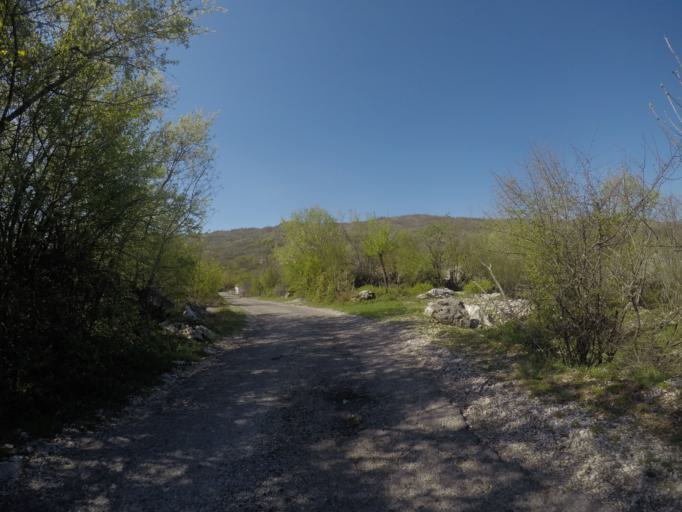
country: ME
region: Danilovgrad
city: Danilovgrad
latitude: 42.5191
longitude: 19.0523
